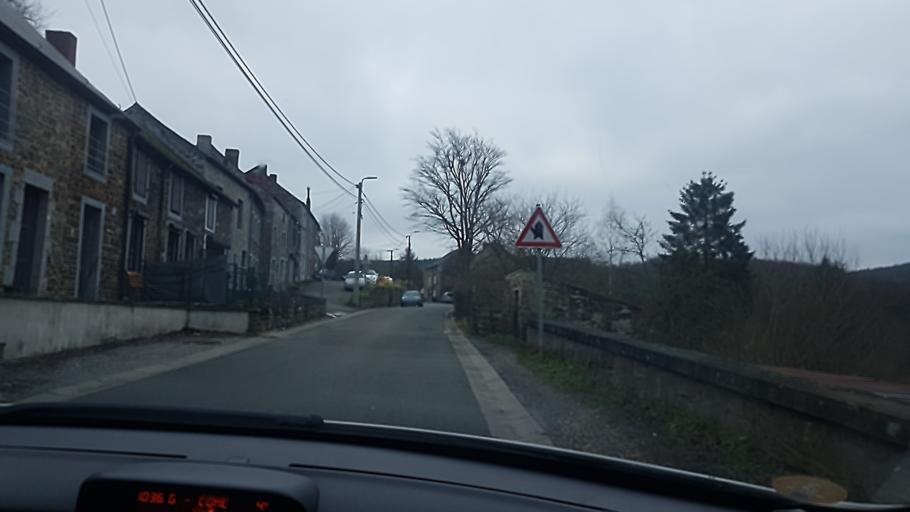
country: BE
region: Wallonia
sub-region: Province de Namur
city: Couvin
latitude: 50.0687
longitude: 4.6069
